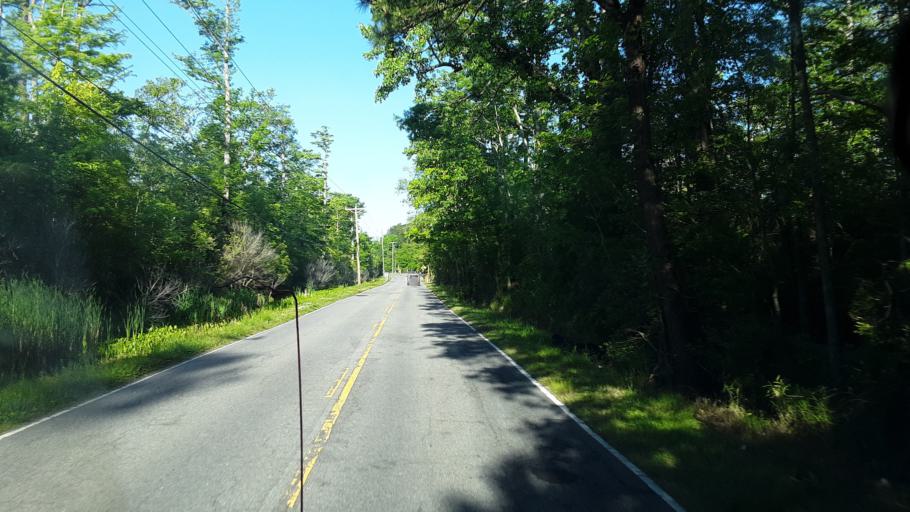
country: US
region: Virginia
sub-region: City of Virginia Beach
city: Virginia Beach
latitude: 36.7216
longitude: -76.0310
